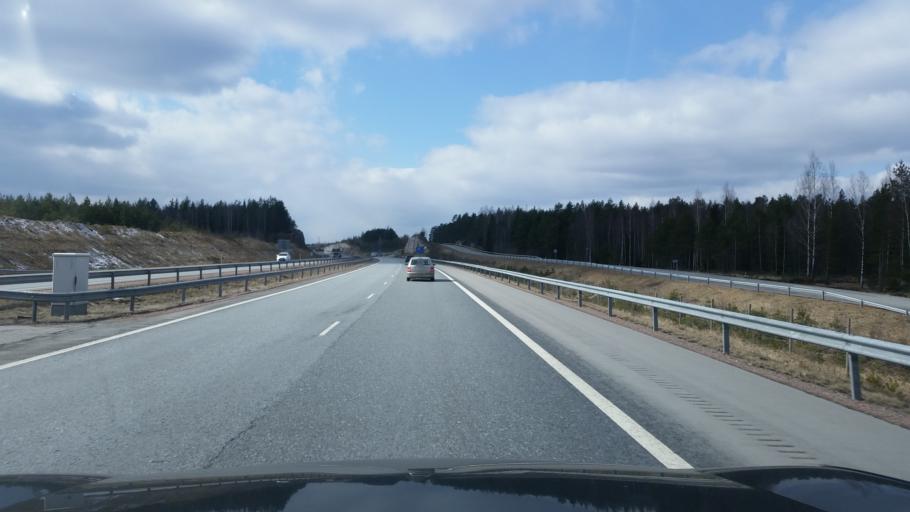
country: FI
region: Varsinais-Suomi
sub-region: Salo
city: Suomusjaervi
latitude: 60.3773
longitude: 23.7304
